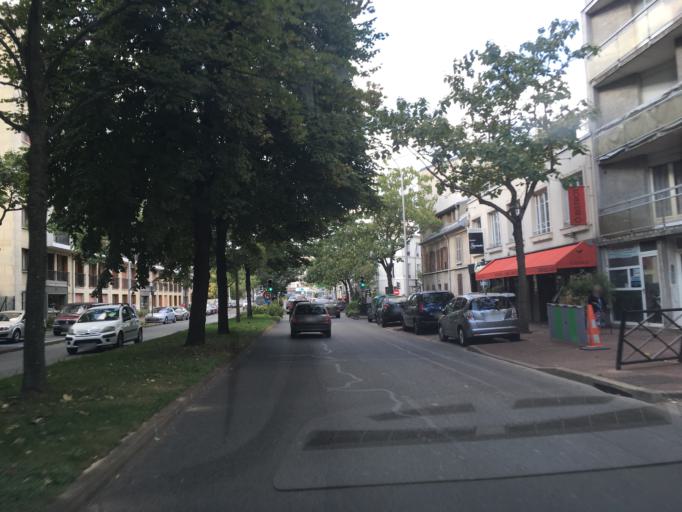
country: FR
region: Ile-de-France
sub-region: Departement du Val-de-Marne
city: Joinville-le-Pont
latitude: 48.8078
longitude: 2.4713
